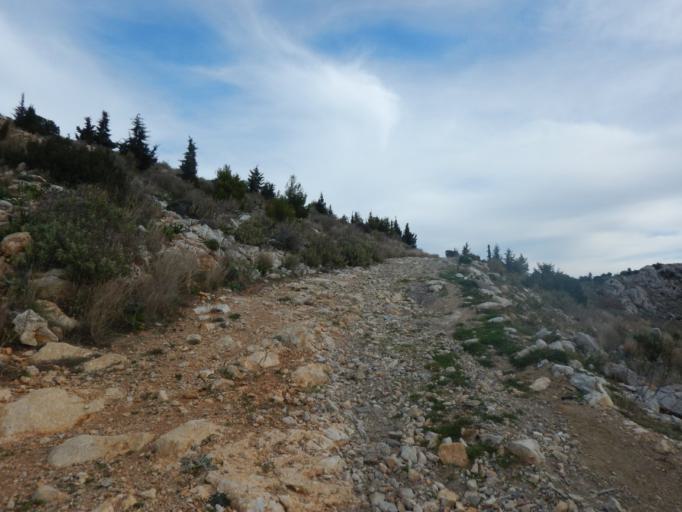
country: GR
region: Attica
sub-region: Nomos Piraios
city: Perama
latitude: 37.9699
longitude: 23.5779
